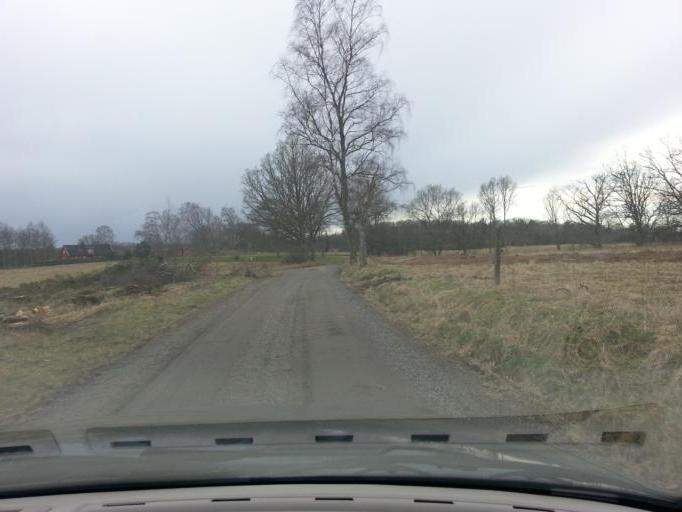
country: SE
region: Skane
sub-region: Klippans Kommun
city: Ljungbyhed
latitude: 56.0882
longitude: 13.2951
